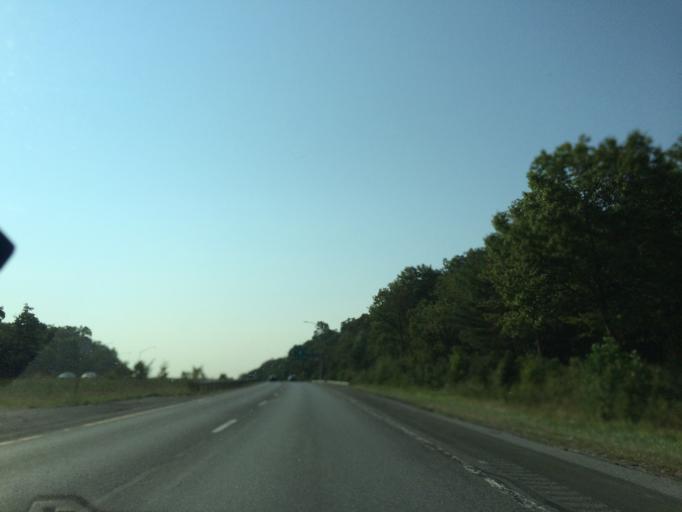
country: US
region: Maryland
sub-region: Howard County
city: Savage
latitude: 39.1446
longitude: -76.8206
